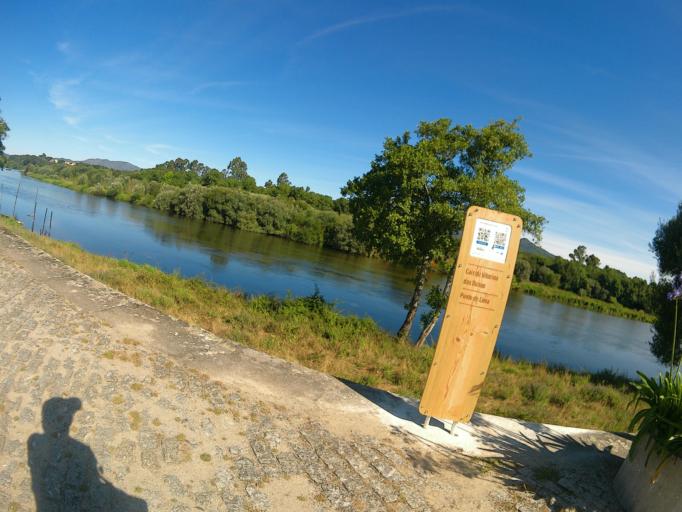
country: PT
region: Viana do Castelo
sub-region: Ponte de Lima
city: Ponte de Lima
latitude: 41.7364
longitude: -8.6523
